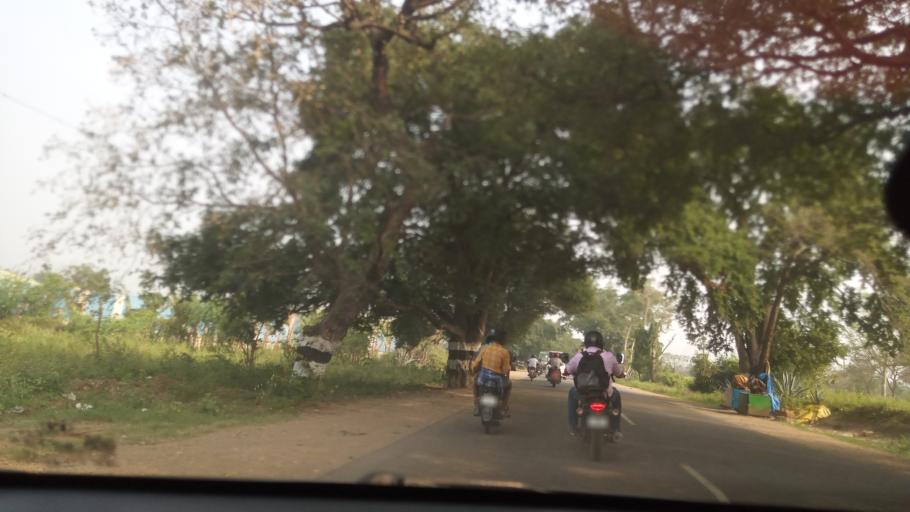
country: IN
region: Tamil Nadu
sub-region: Coimbatore
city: Annur
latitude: 11.1576
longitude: 77.0504
